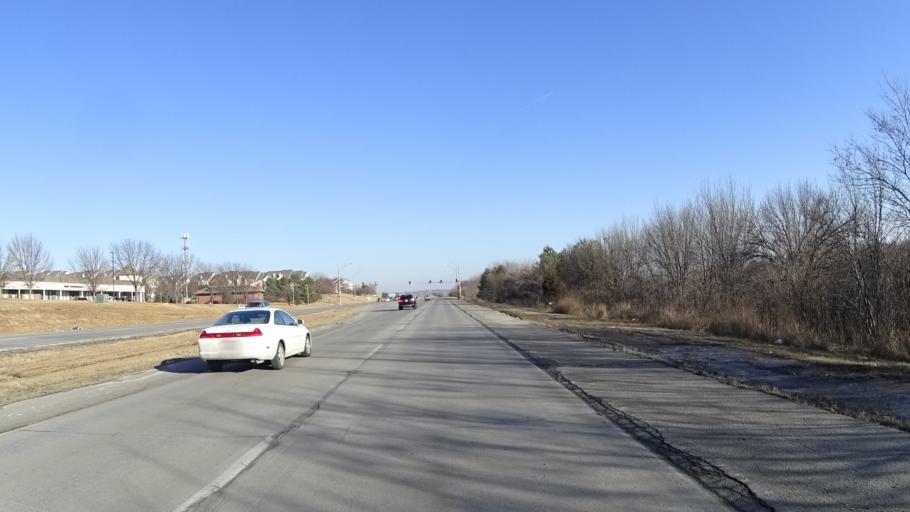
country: US
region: Nebraska
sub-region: Douglas County
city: Bennington
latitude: 41.2920
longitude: -96.1362
